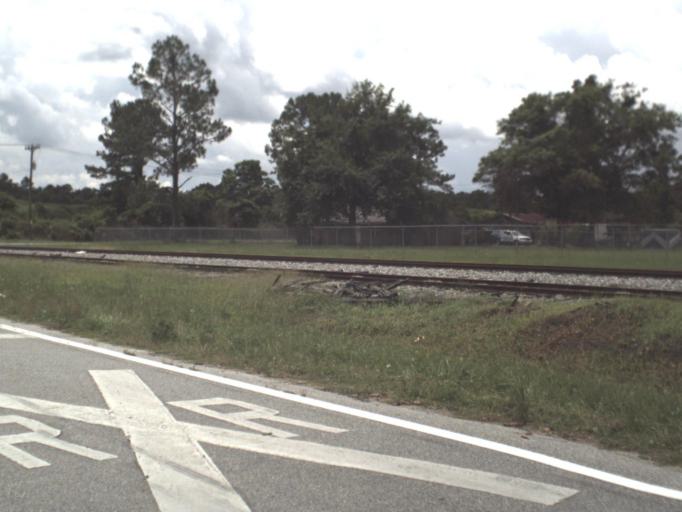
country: US
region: Florida
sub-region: Columbia County
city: Watertown
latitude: 30.1693
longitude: -82.5794
